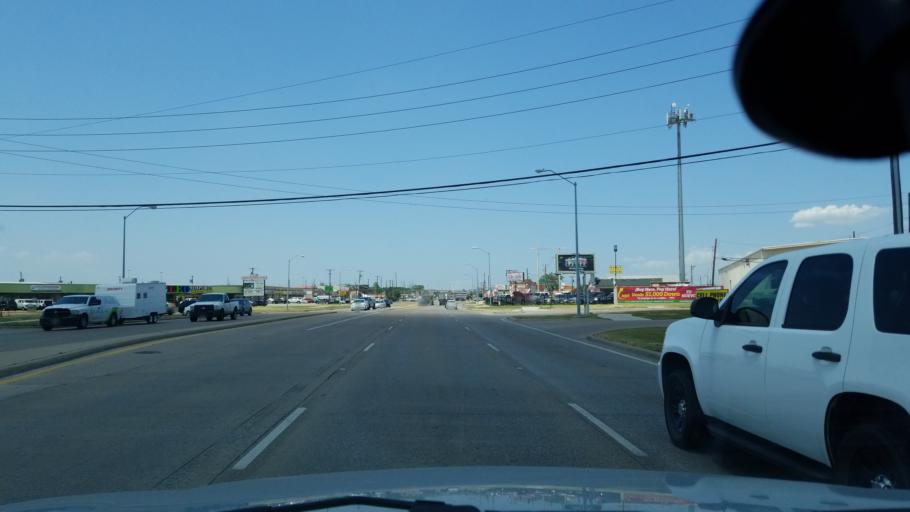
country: US
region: Texas
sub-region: Dallas County
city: Farmers Branch
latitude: 32.8922
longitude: -96.8901
